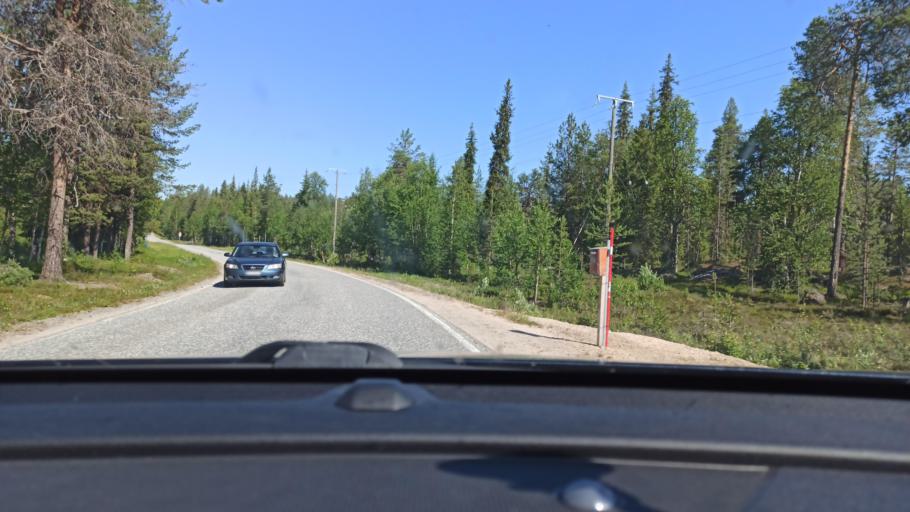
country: FI
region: Lapland
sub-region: Tunturi-Lappi
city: Kolari
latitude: 67.6336
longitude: 24.1601
